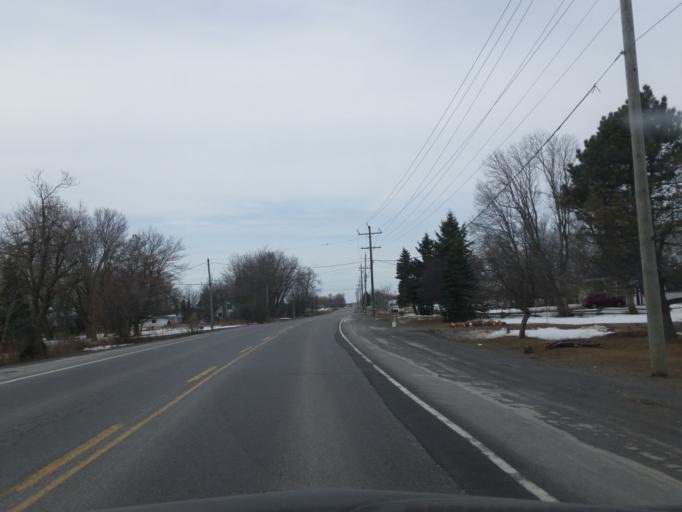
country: CA
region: Ontario
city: Skatepark
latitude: 44.2498
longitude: -76.7981
